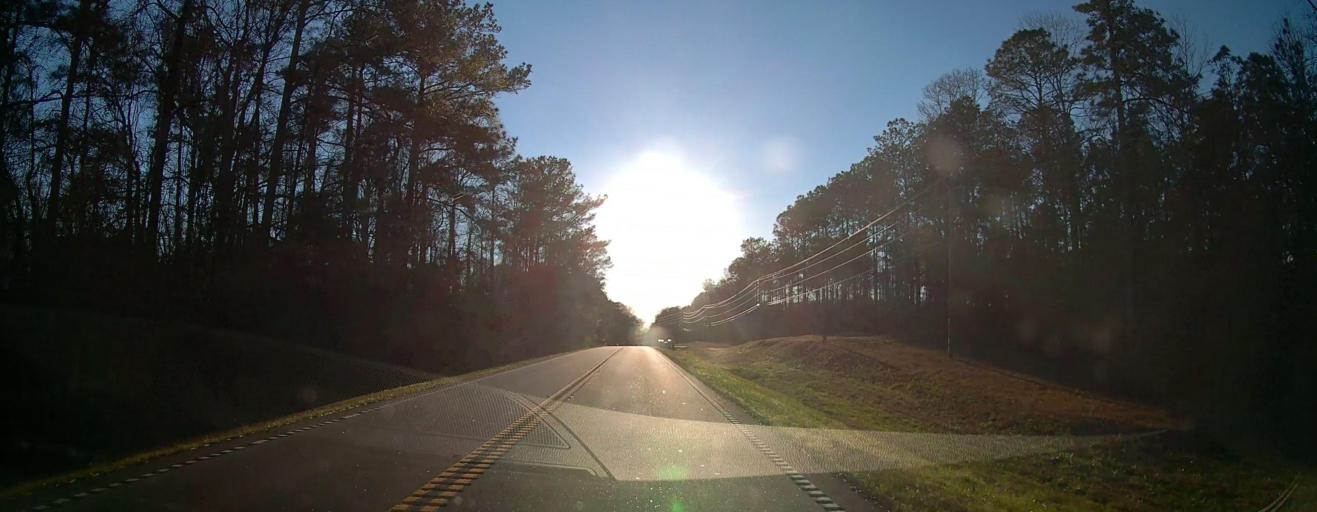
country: US
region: Georgia
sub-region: Harris County
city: Hamilton
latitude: 32.6279
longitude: -84.7803
